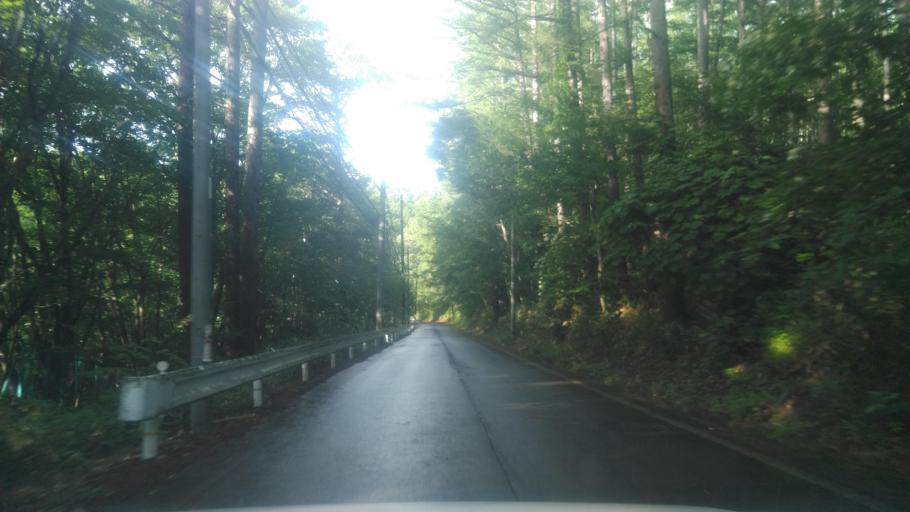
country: JP
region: Nagano
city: Suzaka
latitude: 36.5199
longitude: 138.3551
